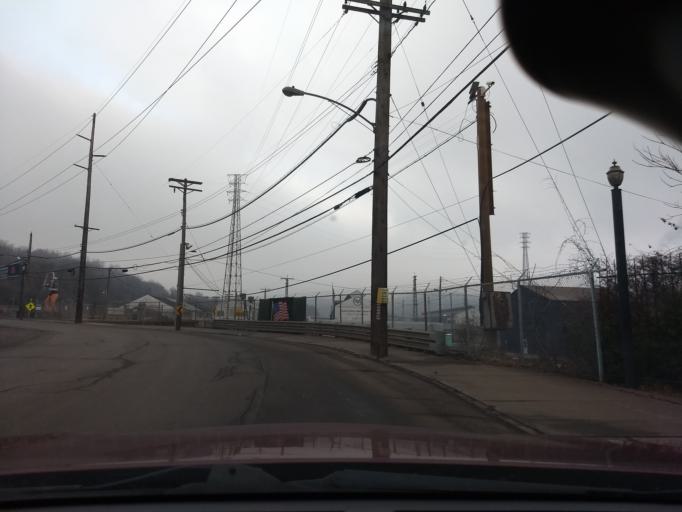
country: US
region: Pennsylvania
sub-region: Allegheny County
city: Braddock
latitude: 40.3972
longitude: -79.8593
